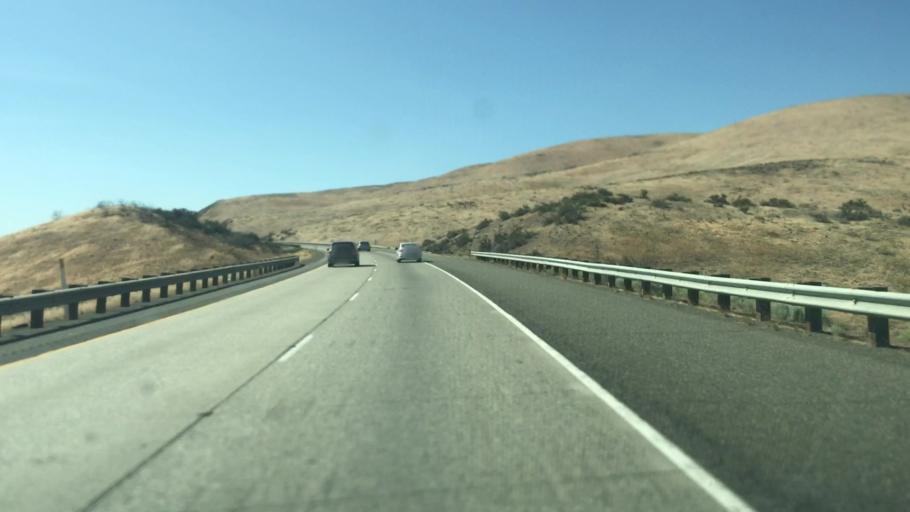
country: US
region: Washington
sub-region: Kittitas County
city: Kittitas
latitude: 46.8604
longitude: -120.3950
